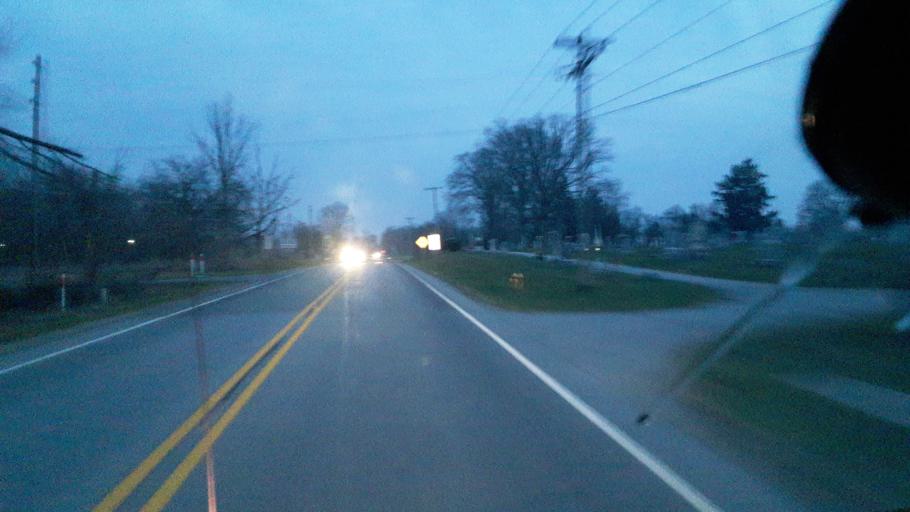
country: US
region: Indiana
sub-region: LaGrange County
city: Lagrange
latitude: 41.6319
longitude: -85.4163
